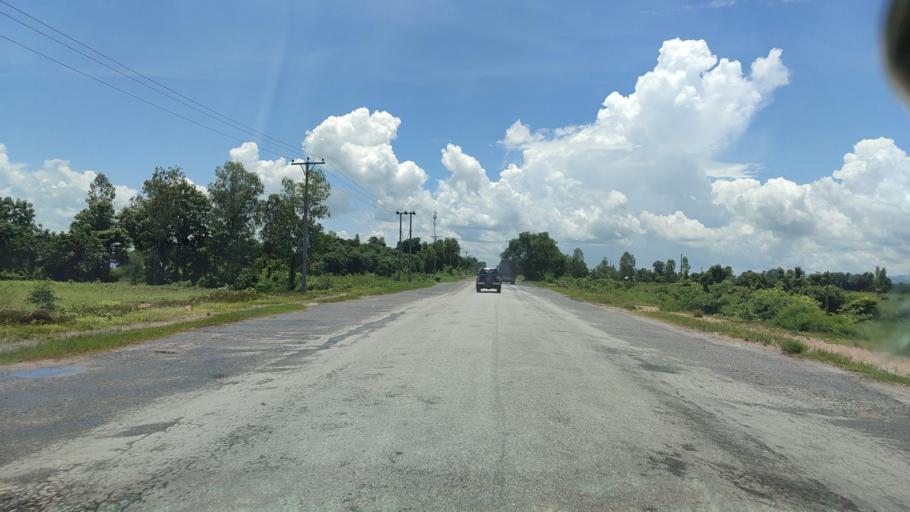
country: MM
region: Bago
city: Pyu
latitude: 18.6614
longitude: 96.4112
